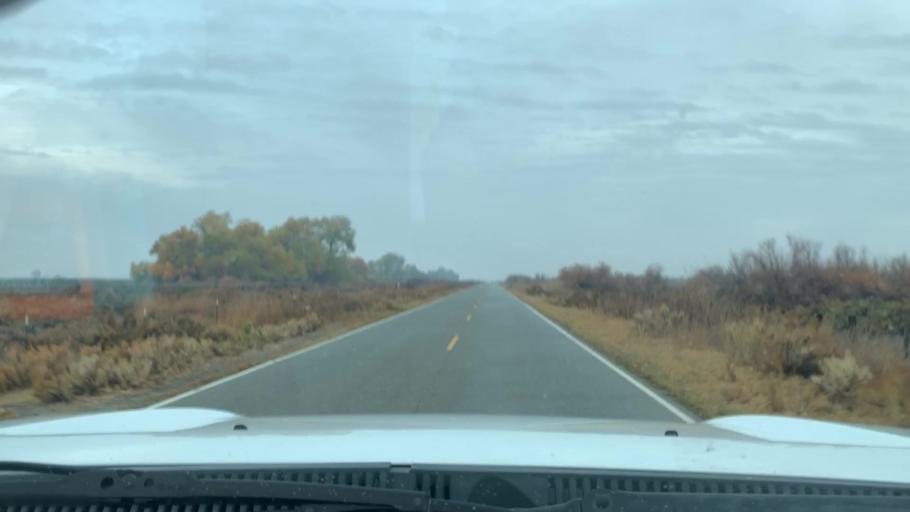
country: US
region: California
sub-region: Kern County
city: Lost Hills
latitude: 35.7247
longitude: -119.5794
